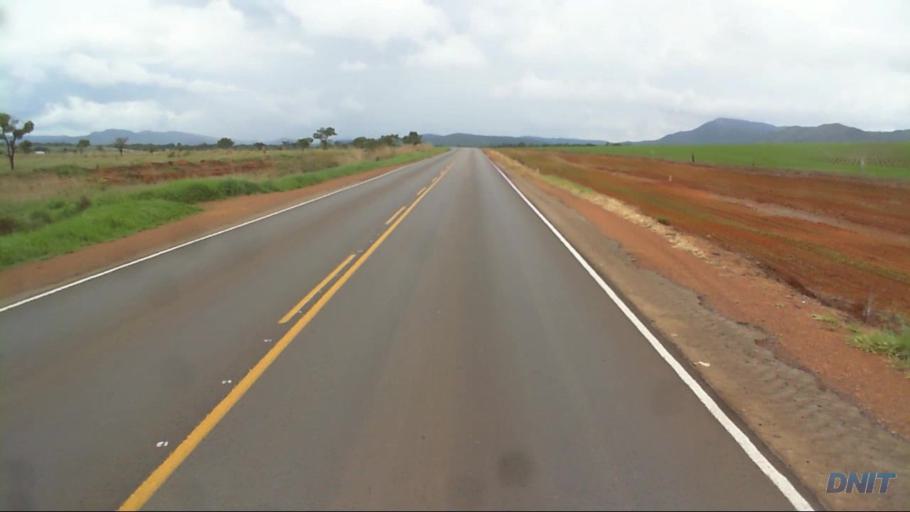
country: BR
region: Goias
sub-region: Padre Bernardo
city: Padre Bernardo
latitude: -15.3378
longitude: -48.2338
